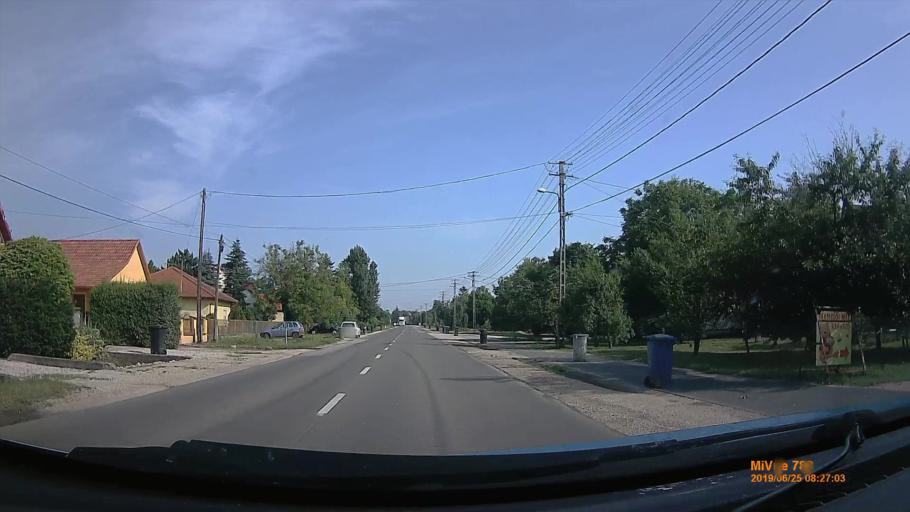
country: HU
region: Fejer
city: Szabadbattyan
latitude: 47.1101
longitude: 18.3817
